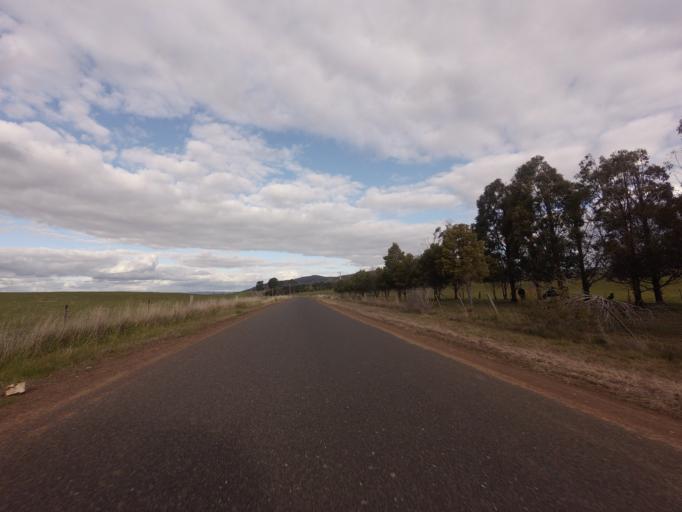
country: AU
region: Tasmania
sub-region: Northern Midlands
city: Evandale
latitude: -41.9015
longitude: 147.3513
